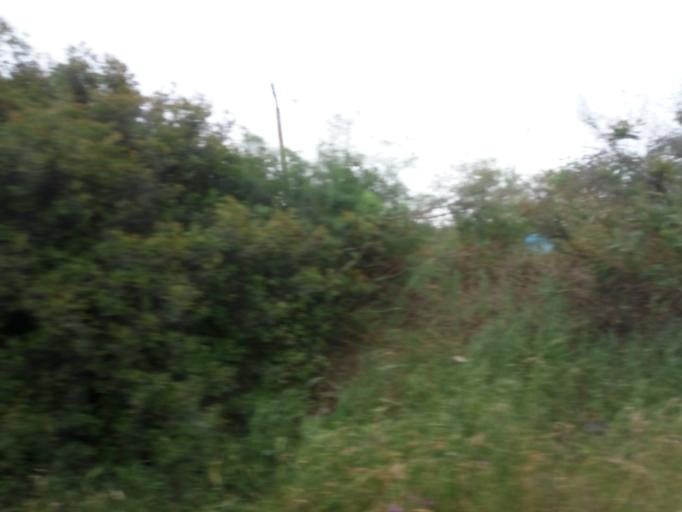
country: DZ
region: Tipaza
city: Tipasa
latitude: 36.5766
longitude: 2.5476
